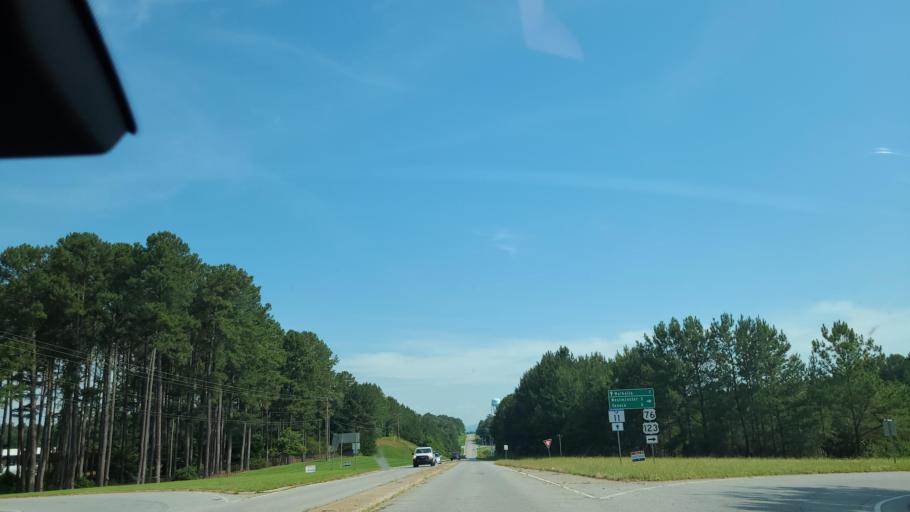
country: US
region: South Carolina
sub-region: Oconee County
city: Westminster
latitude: 34.6656
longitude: -83.0393
